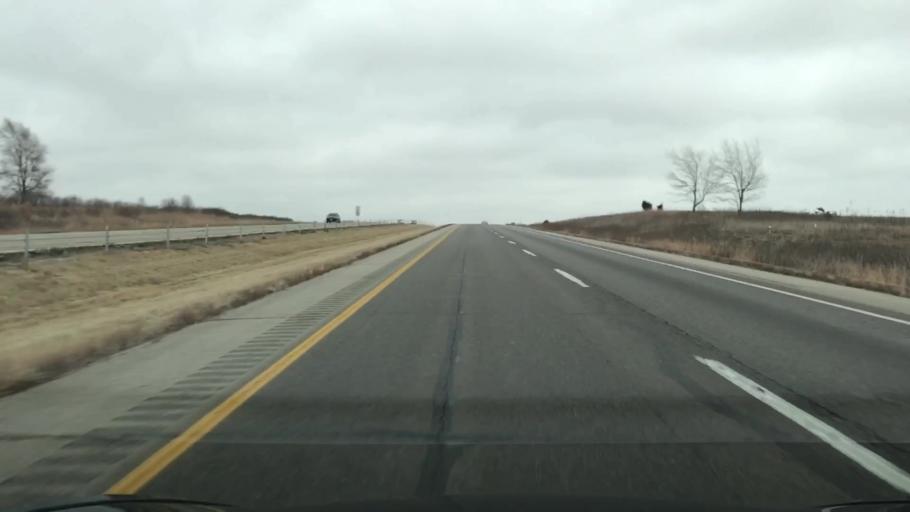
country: US
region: Iowa
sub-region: Guthrie County
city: Stuart
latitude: 41.4930
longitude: -94.2553
